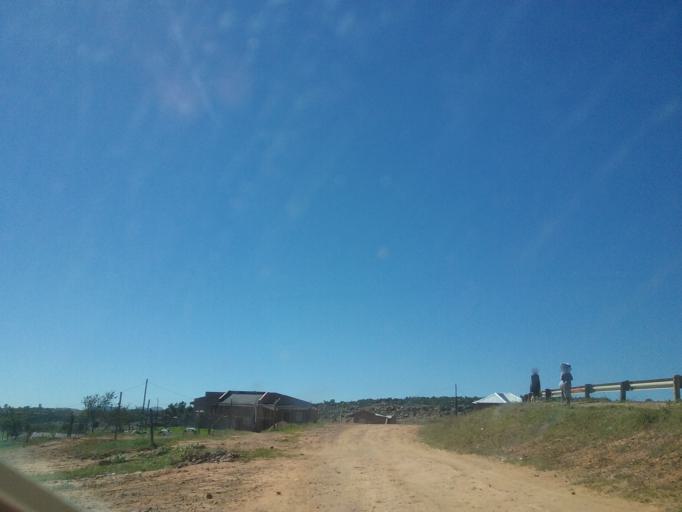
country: LS
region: Maseru
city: Maseru
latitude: -29.4020
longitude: 27.5726
